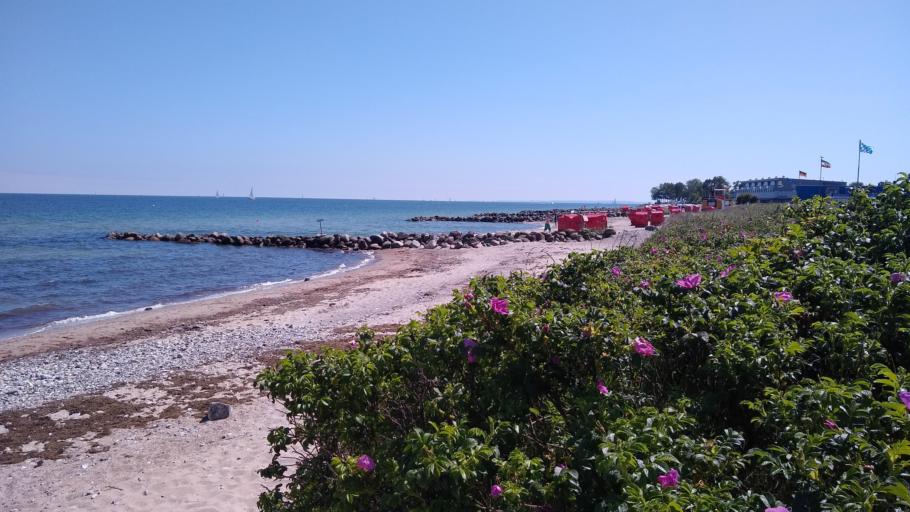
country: DE
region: Schleswig-Holstein
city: Brodersby
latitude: 54.6366
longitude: 10.0307
